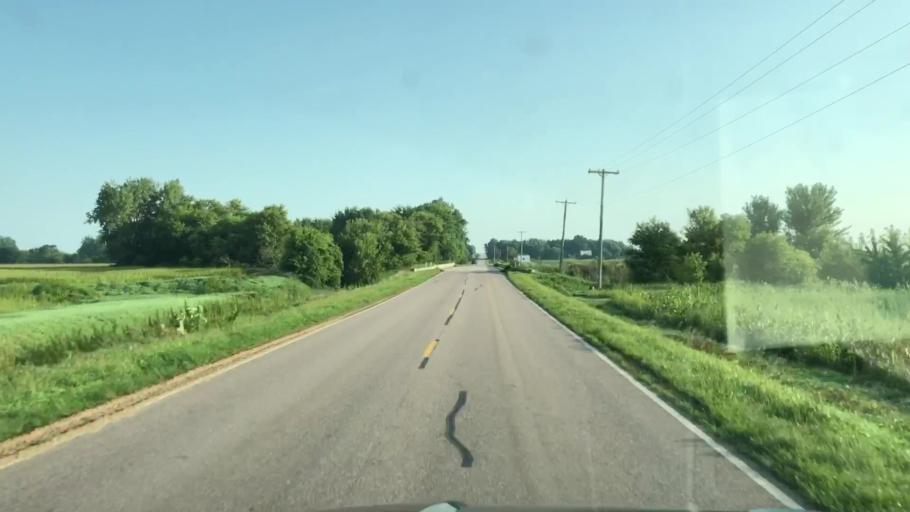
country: US
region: Iowa
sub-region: Lyon County
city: George
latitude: 43.2473
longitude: -96.0004
